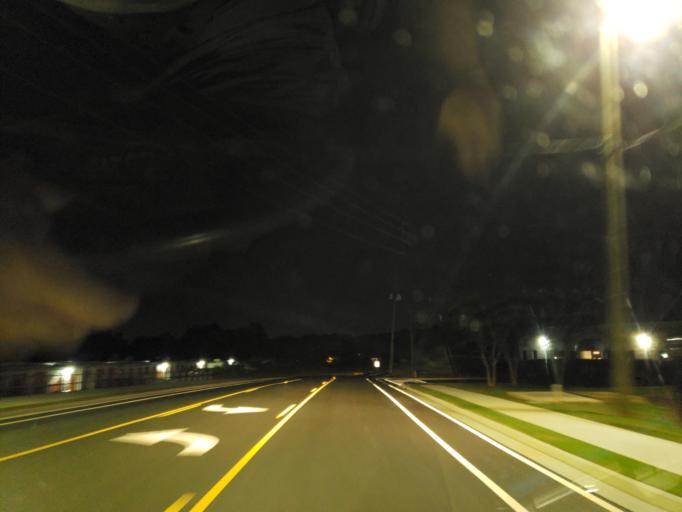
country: US
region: Georgia
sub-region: Fulton County
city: Roswell
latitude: 34.0494
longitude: -84.3349
